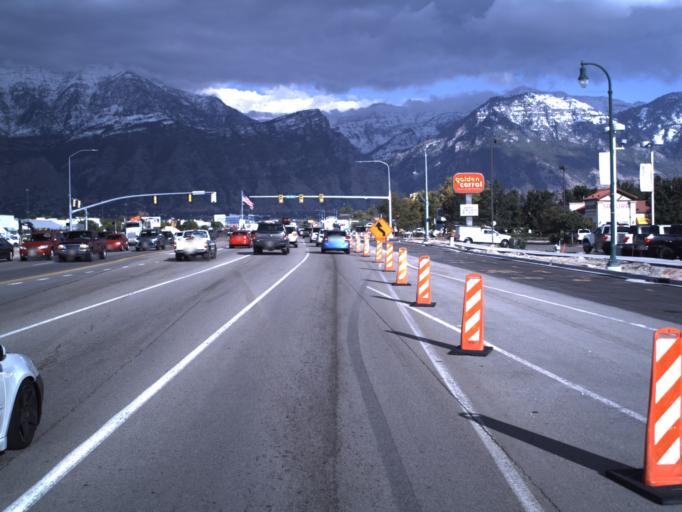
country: US
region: Utah
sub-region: Utah County
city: Orem
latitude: 40.2735
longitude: -111.7019
